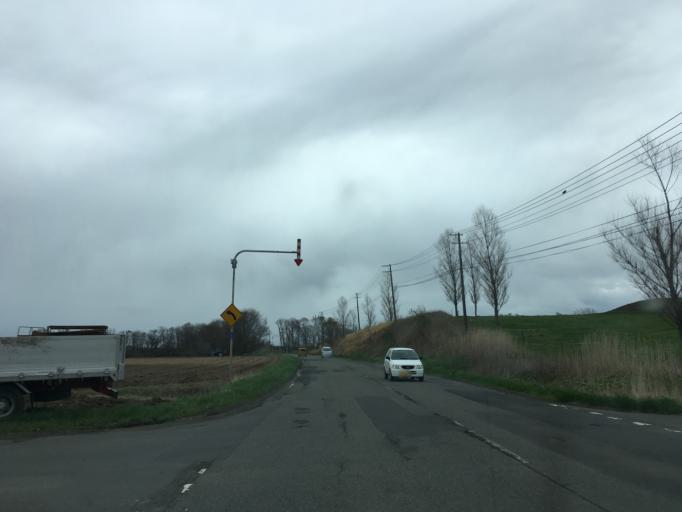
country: JP
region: Hokkaido
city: Chitose
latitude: 42.8973
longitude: 141.8137
